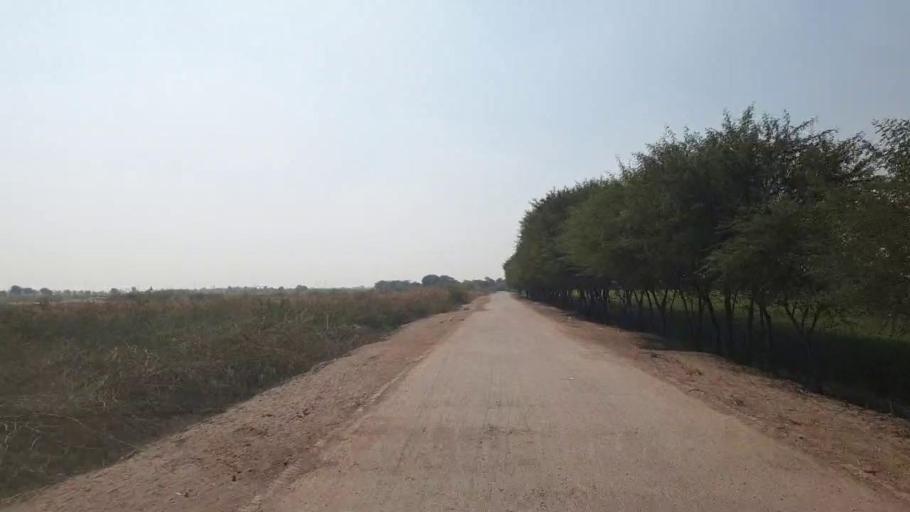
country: PK
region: Sindh
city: Chambar
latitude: 25.3864
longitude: 68.9234
